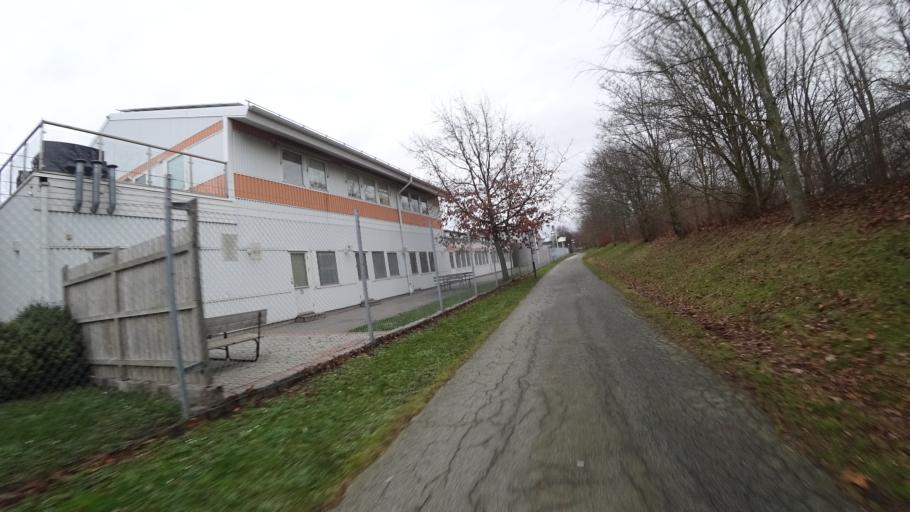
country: SE
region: Skane
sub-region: Malmo
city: Bunkeflostrand
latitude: 55.5736
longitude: 12.9326
